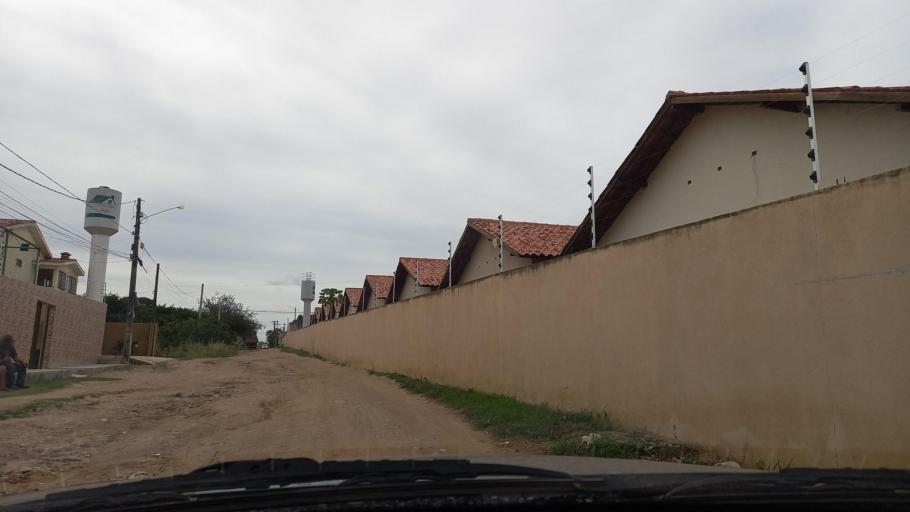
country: BR
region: Pernambuco
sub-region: Gravata
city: Gravata
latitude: -8.1997
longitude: -35.5941
